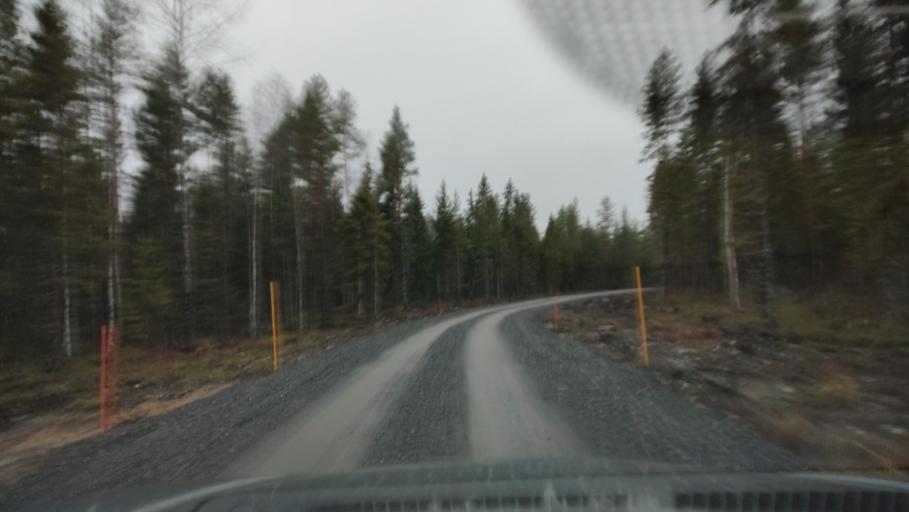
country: FI
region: Southern Ostrobothnia
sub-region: Suupohja
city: Karijoki
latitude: 62.1594
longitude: 21.5923
